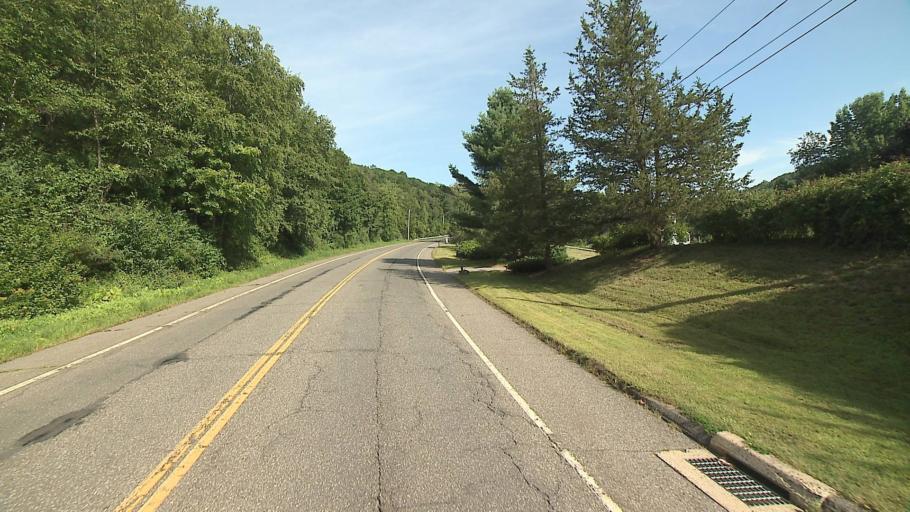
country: US
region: Connecticut
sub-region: Litchfield County
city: Thomaston
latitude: 41.6764
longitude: -73.0910
